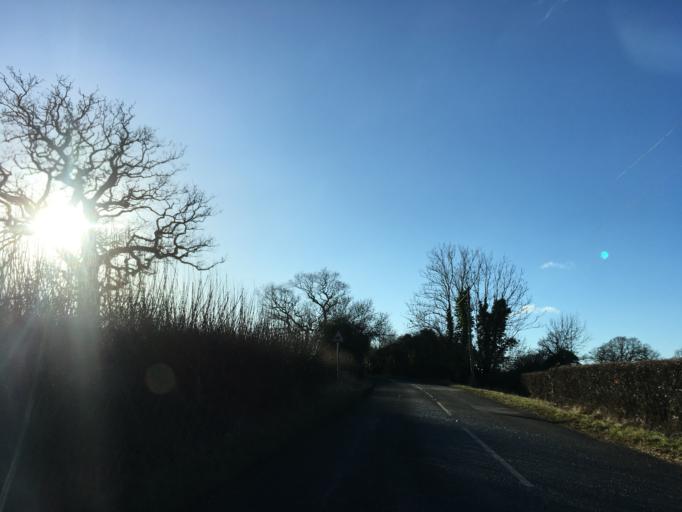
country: GB
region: England
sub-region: Wiltshire
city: Luckington
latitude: 51.5327
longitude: -2.2626
